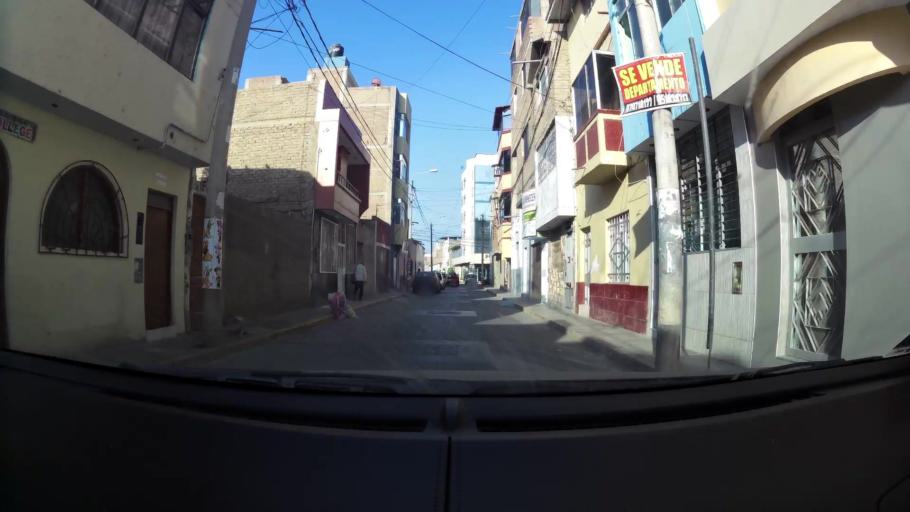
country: PE
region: Lambayeque
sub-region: Provincia de Chiclayo
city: Chiclayo
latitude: -6.7748
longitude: -79.8364
